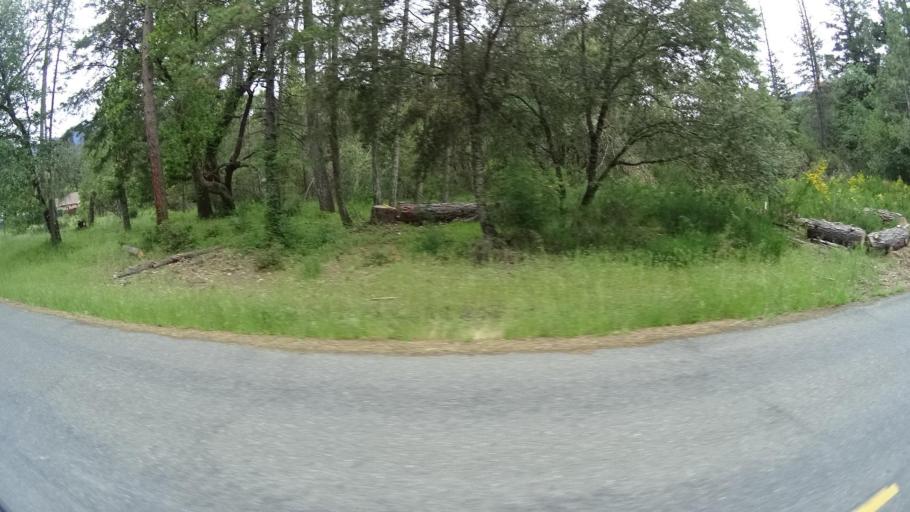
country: US
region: California
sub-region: Humboldt County
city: Willow Creek
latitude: 40.9473
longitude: -123.6275
